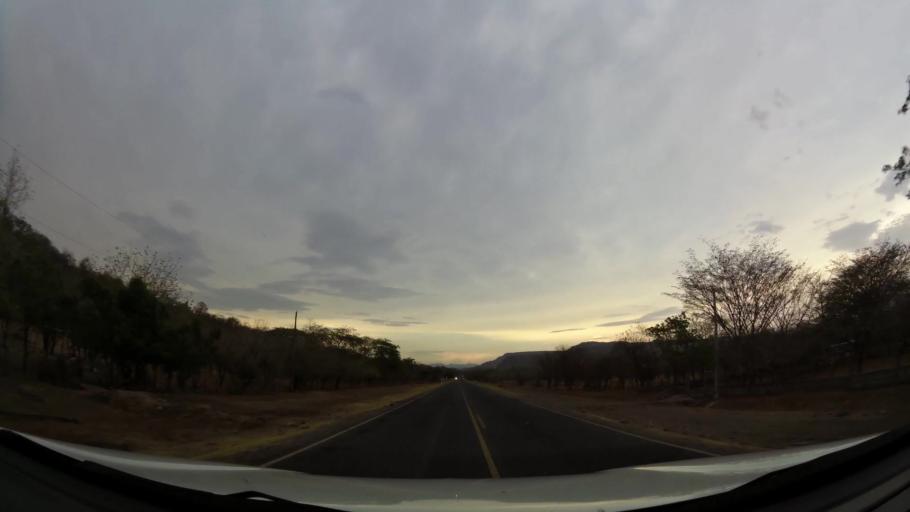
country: NI
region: Leon
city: La Jicaral
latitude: 12.6700
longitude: -86.4344
